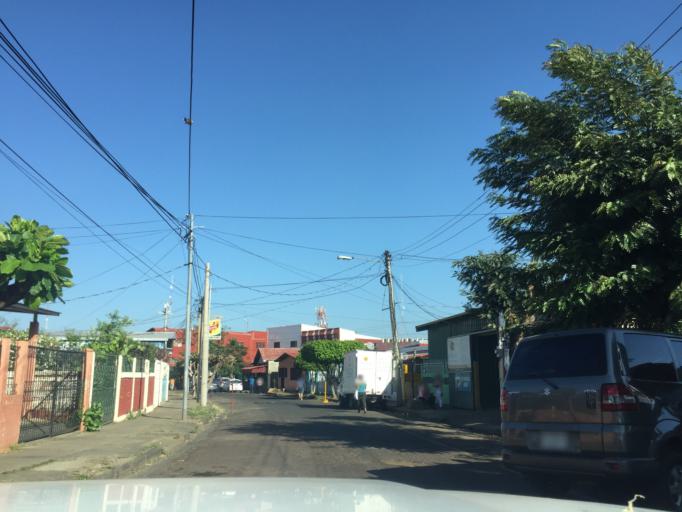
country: NI
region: Managua
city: Managua
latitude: 12.1460
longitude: -86.2566
